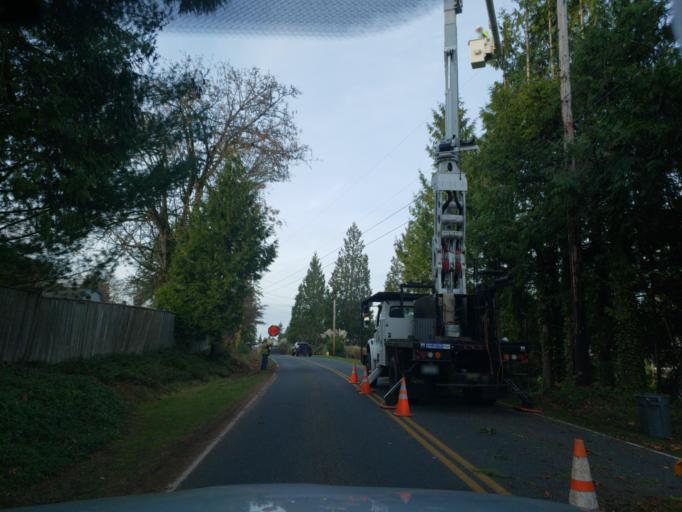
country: US
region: Washington
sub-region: Snohomish County
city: Cathcart
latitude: 47.8644
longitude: -122.0944
